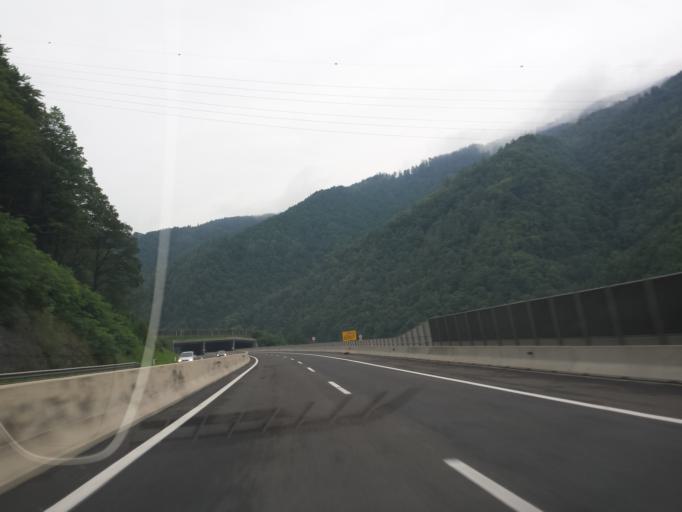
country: AT
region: Styria
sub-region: Politischer Bezirk Bruck-Muerzzuschlag
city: Bruck an der Mur
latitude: 47.3857
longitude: 15.3089
